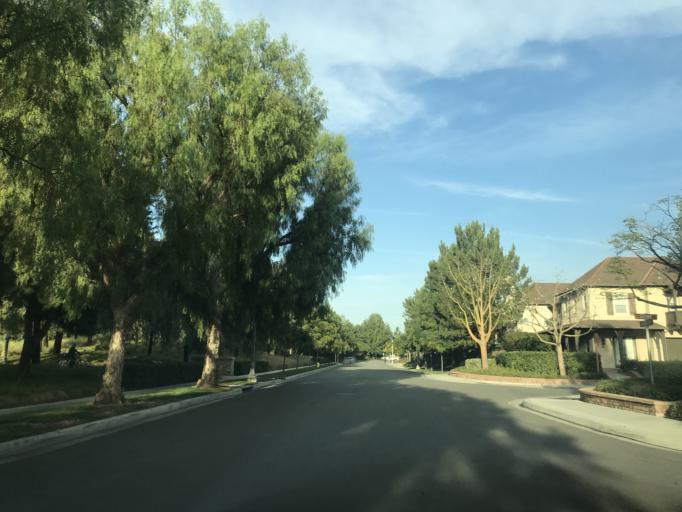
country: US
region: California
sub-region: Orange County
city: North Tustin
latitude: 33.7050
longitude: -117.7515
